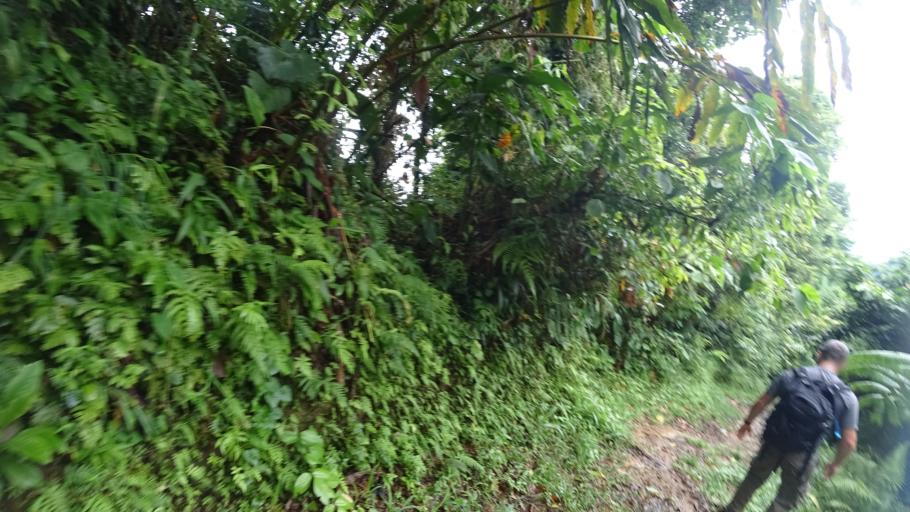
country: PH
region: Eastern Visayas
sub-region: Province of Leyte
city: Bugho
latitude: 10.8276
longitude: 124.8726
